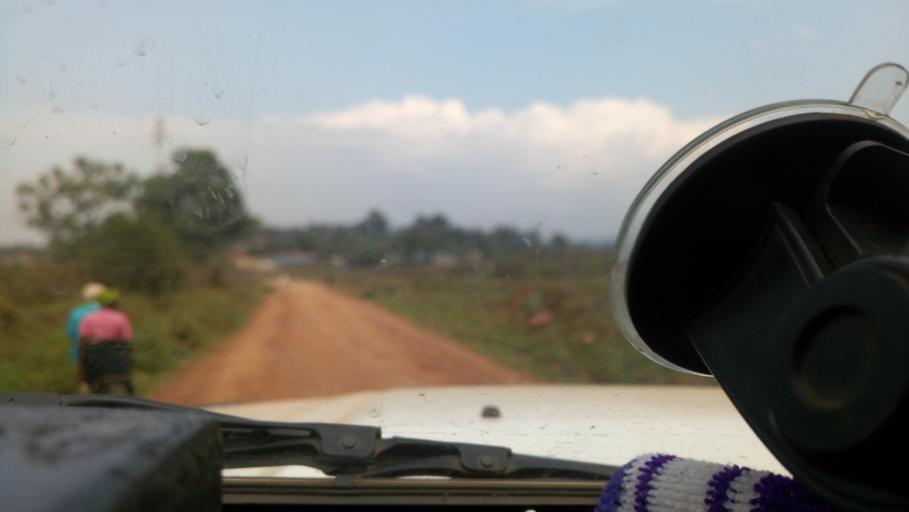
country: KE
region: Kericho
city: Litein
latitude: -0.6249
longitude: 35.1999
